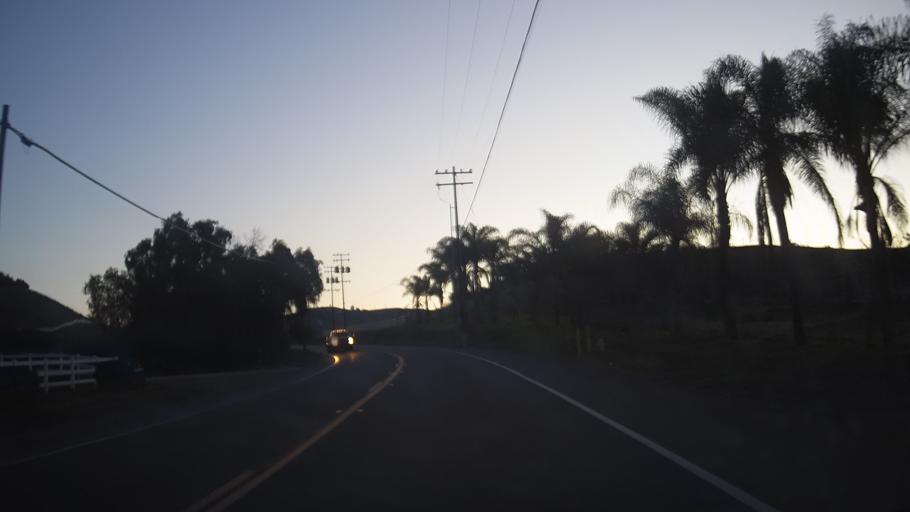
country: US
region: California
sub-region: San Diego County
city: Harbison Canyon
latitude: 32.7902
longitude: -116.8370
